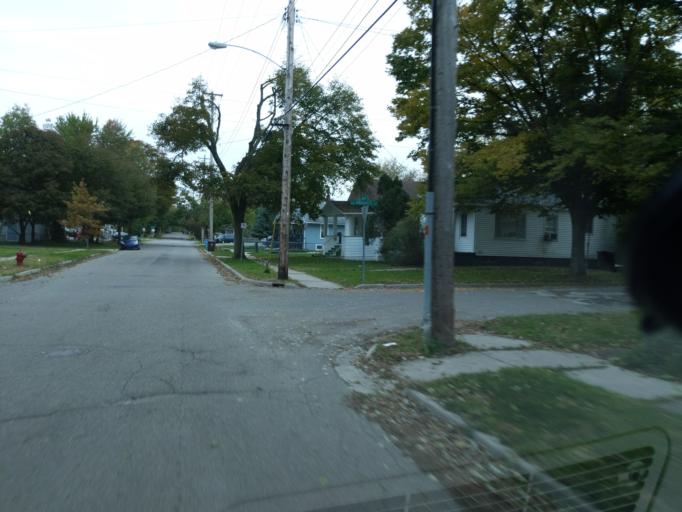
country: US
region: Michigan
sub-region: Ingham County
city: East Lansing
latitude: 42.7312
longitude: -84.5164
